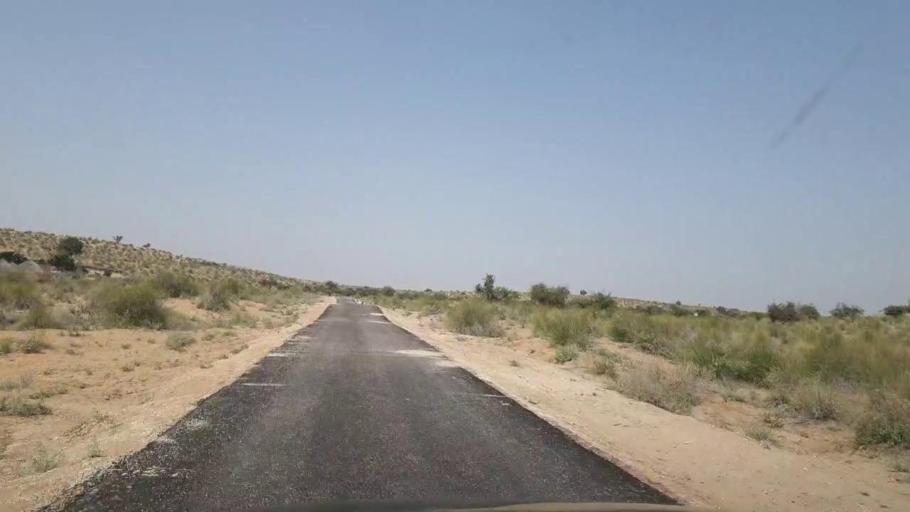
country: PK
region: Sindh
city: Islamkot
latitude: 25.1197
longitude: 70.6518
